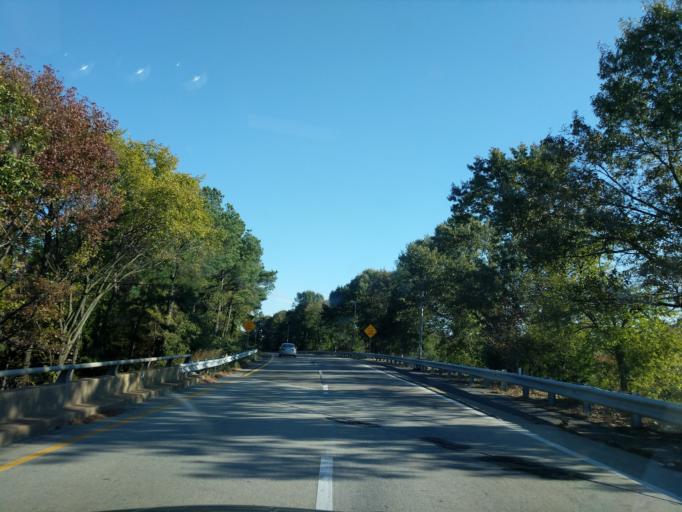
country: US
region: Virginia
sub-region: Henrico County
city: Lakeside
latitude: 37.5878
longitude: -77.4702
